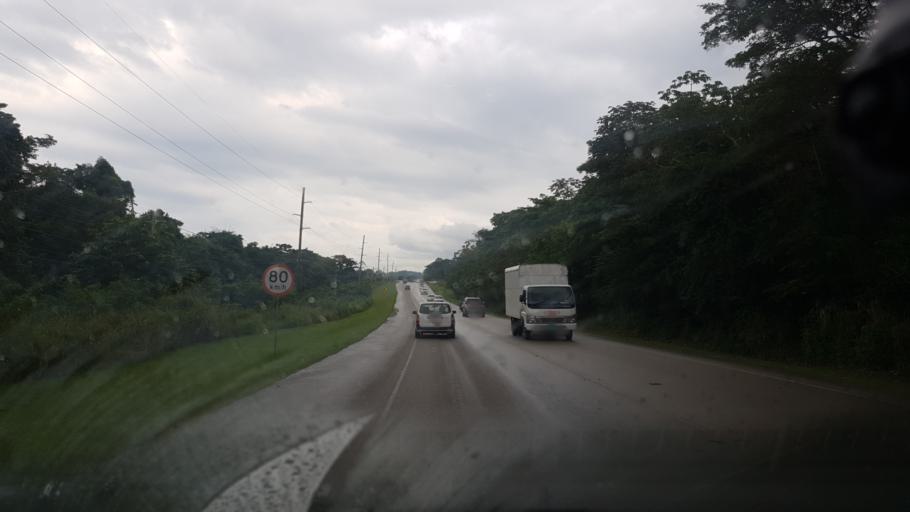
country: JM
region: Saint Ann
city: Saint Ann's Bay
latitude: 18.4283
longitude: -77.1851
